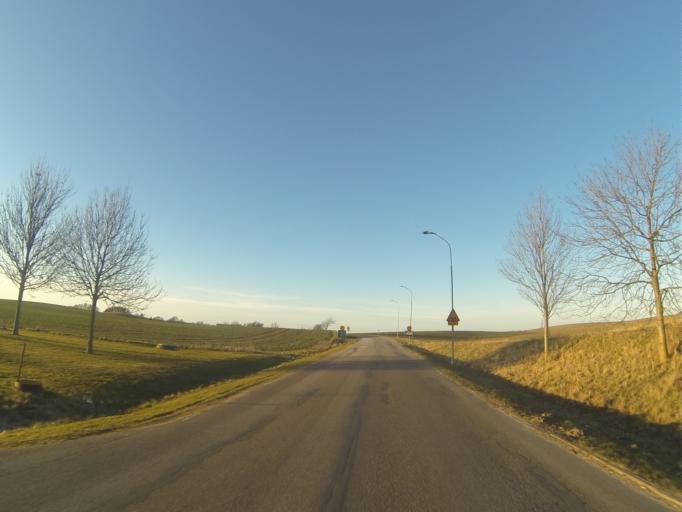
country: SE
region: Skane
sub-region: Staffanstorps Kommun
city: Staffanstorp
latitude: 55.5880
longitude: 13.1835
